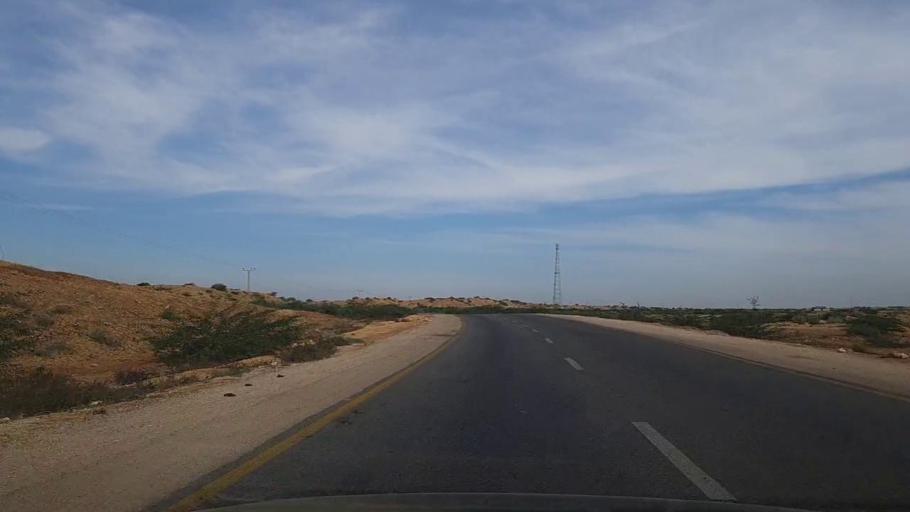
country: PK
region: Sindh
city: Thatta
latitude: 24.8598
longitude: 68.0238
